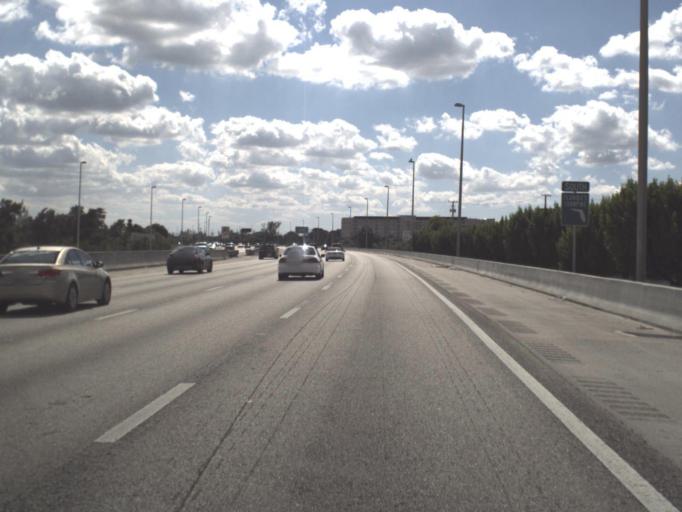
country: US
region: Florida
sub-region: Broward County
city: Lauderdale Lakes
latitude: 26.1824
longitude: -80.2183
